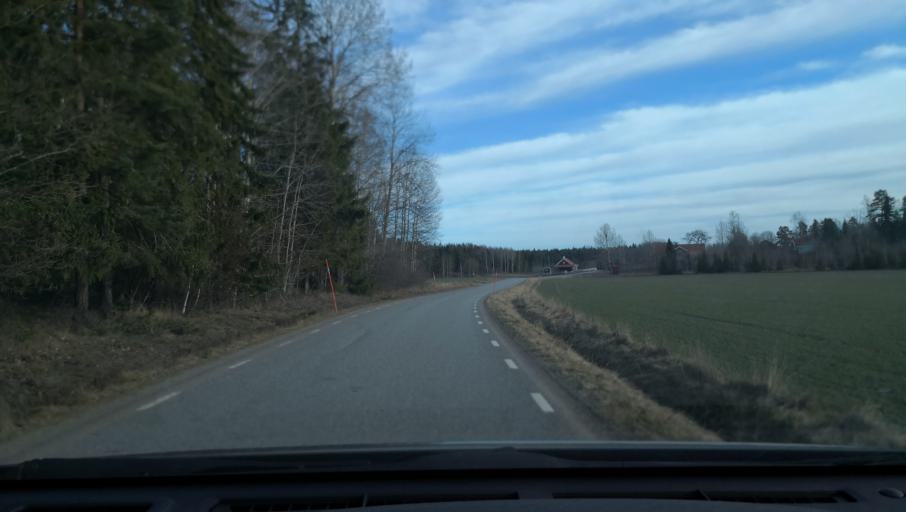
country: SE
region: Uppsala
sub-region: Enkopings Kommun
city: Grillby
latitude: 59.5429
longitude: 17.1620
